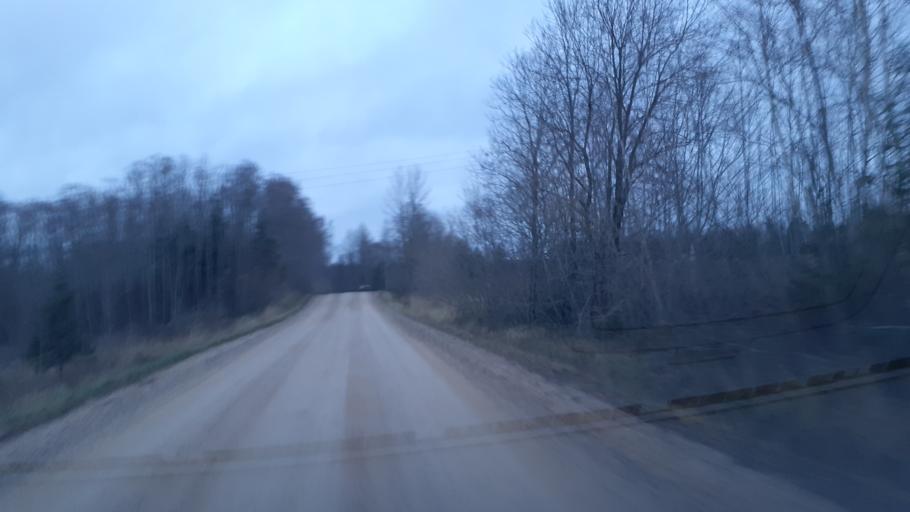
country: LV
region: Kuldigas Rajons
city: Kuldiga
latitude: 56.9845
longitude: 22.0502
